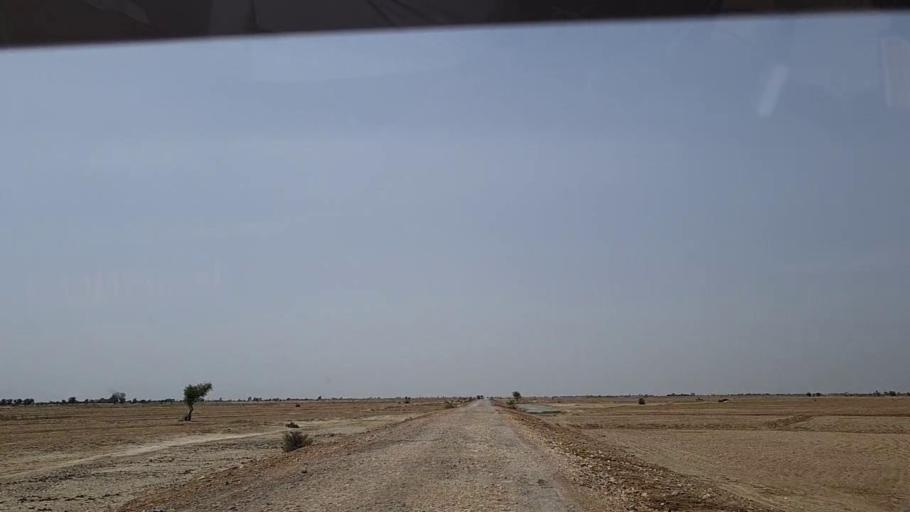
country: PK
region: Sindh
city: Johi
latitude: 26.7191
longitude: 67.6465
